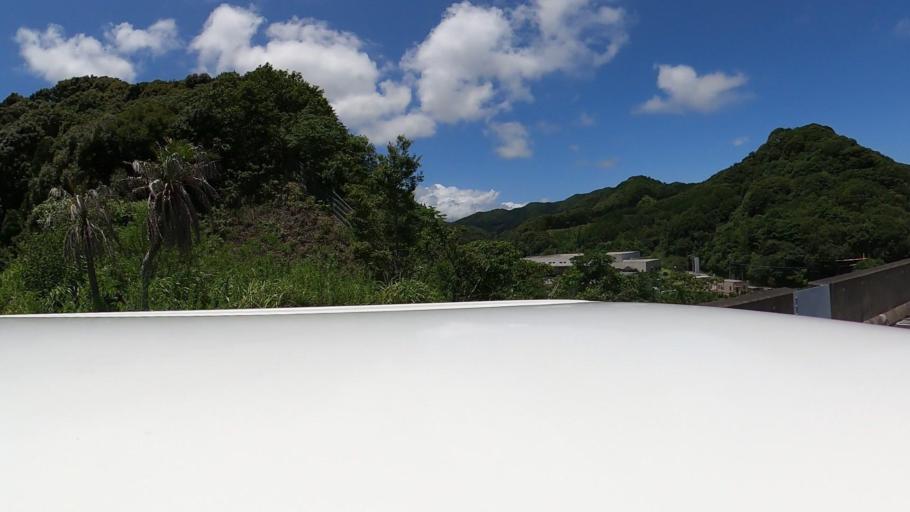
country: JP
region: Miyazaki
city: Nobeoka
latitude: 32.4978
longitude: 131.6603
